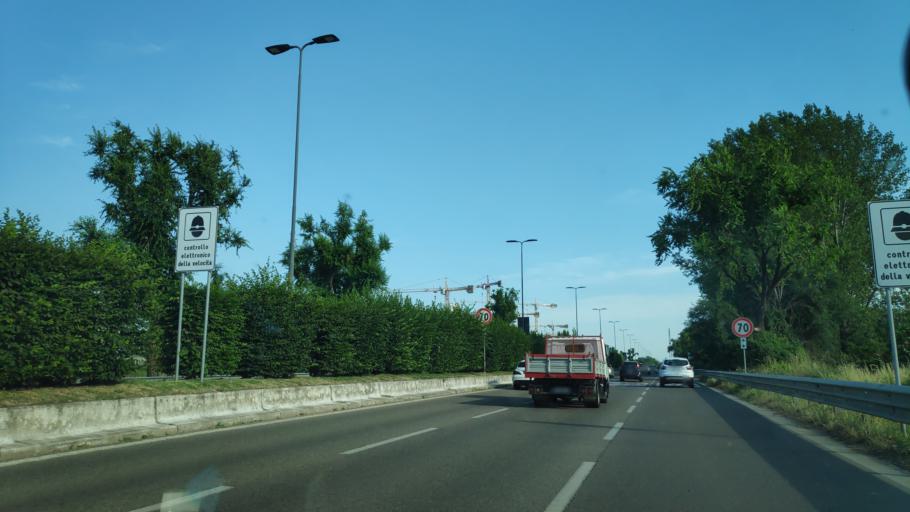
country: IT
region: Lombardy
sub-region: Citta metropolitana di Milano
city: Milano
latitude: 45.4285
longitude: 9.1956
